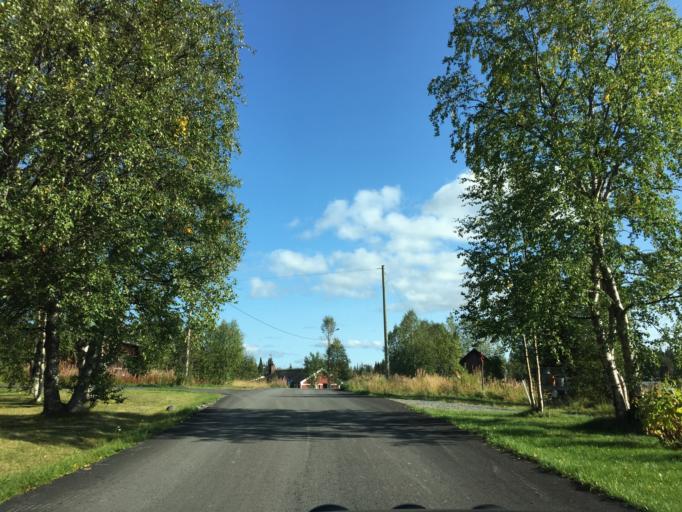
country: SE
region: Norrbotten
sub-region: Gallivare Kommun
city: Malmberget
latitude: 67.6475
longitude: 21.0613
